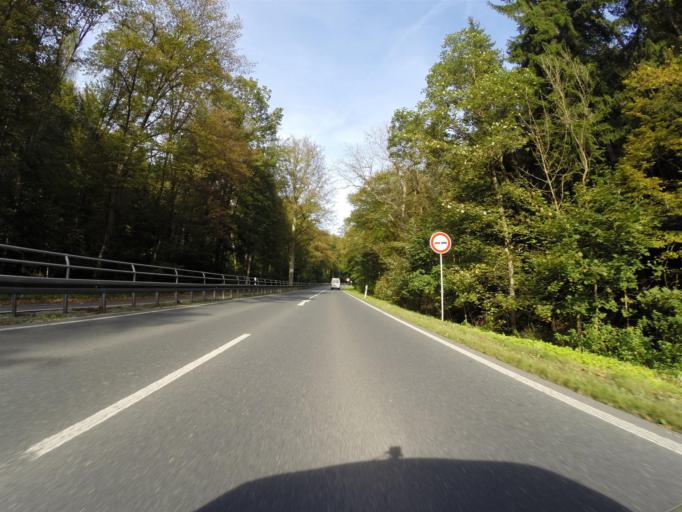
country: DE
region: Thuringia
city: Grossschwabhausen
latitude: 50.9481
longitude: 11.5336
